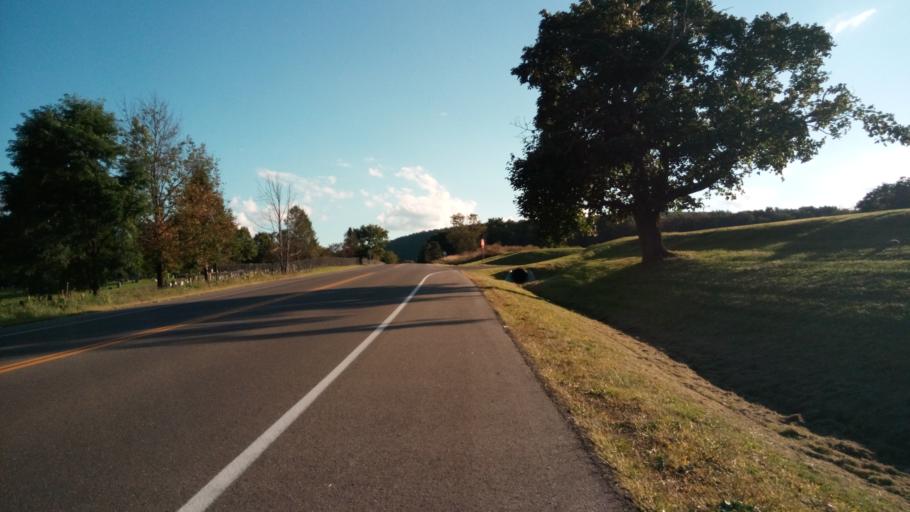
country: US
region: New York
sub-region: Chemung County
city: Elmira Heights
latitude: 42.1121
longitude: -76.8293
